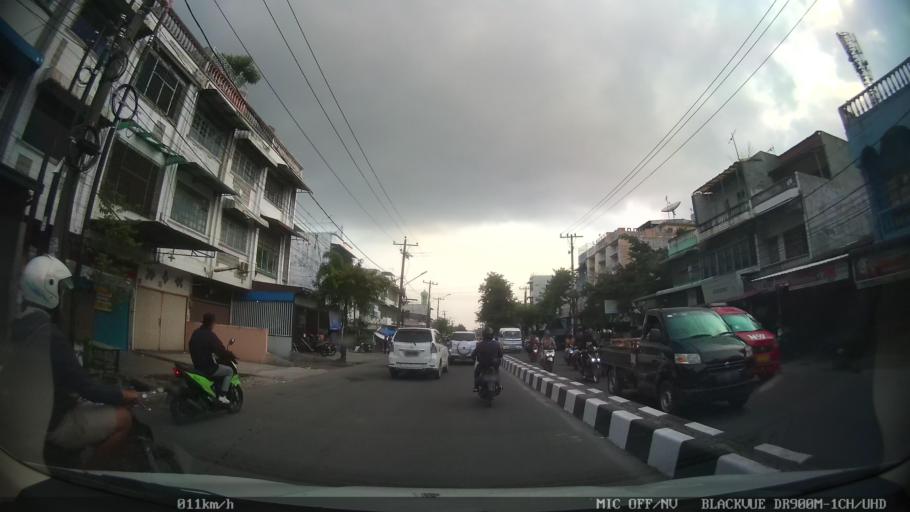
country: ID
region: North Sumatra
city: Medan
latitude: 3.5933
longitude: 98.7116
